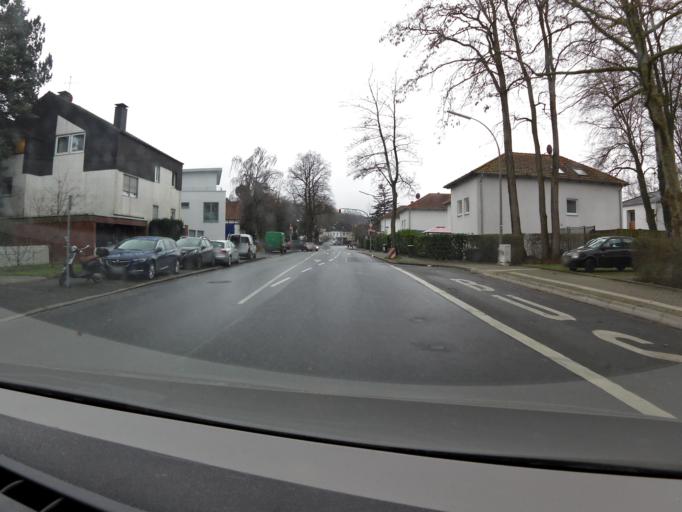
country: DE
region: North Rhine-Westphalia
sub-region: Regierungsbezirk Arnsberg
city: Dortmund
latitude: 51.4628
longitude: 7.4805
